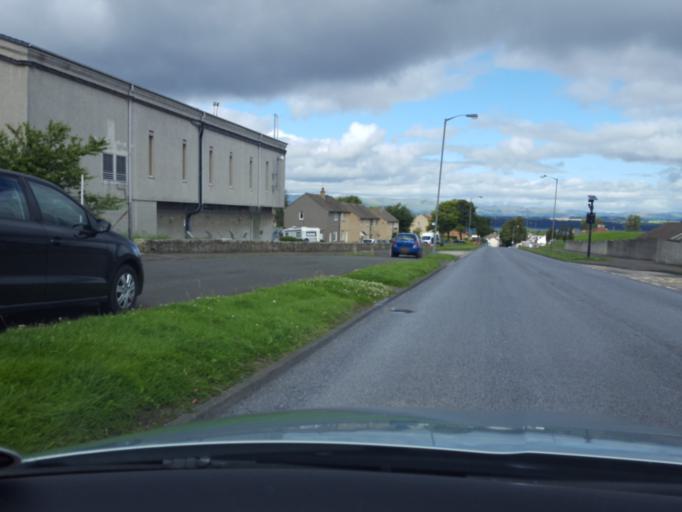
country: GB
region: Scotland
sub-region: Falkirk
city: Bo'ness
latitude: 56.0055
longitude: -3.6100
